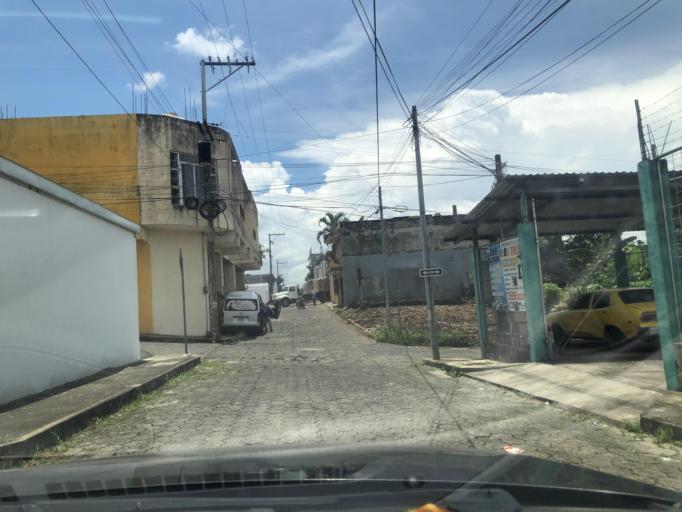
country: GT
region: Quetzaltenango
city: Coatepeque
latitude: 14.7080
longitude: -91.8675
